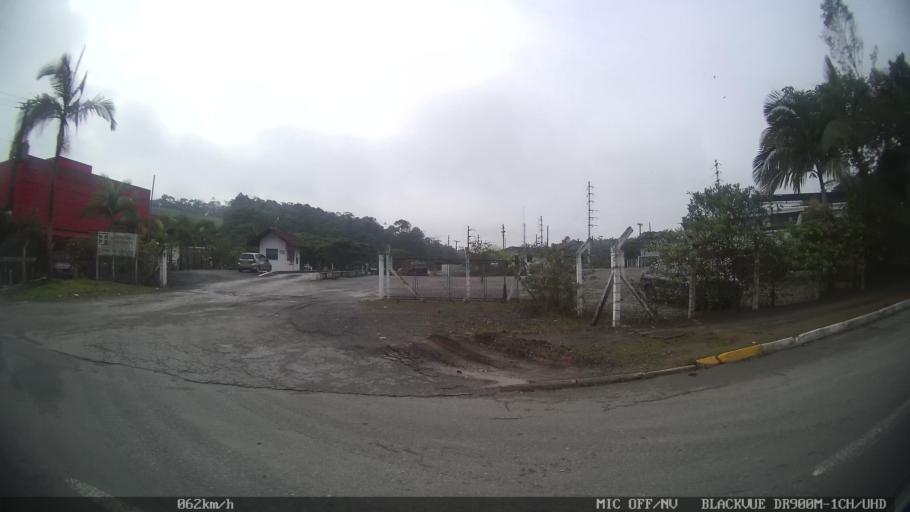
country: BR
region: Santa Catarina
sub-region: Joinville
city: Joinville
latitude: -26.3790
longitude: -48.8436
